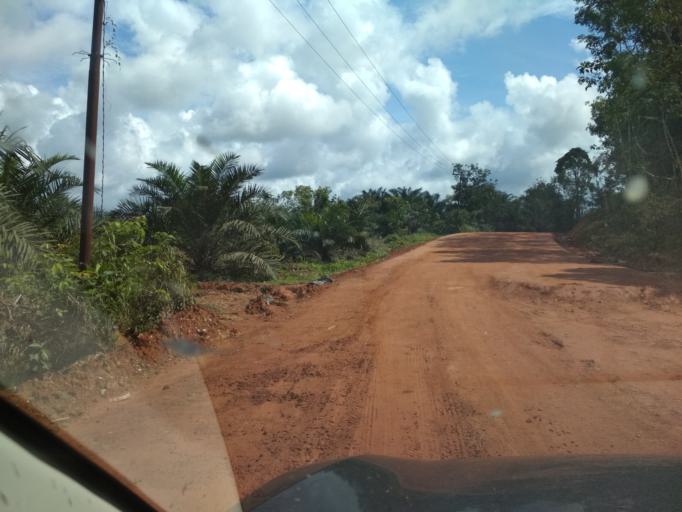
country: ID
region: West Kalimantan
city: Tayan
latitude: 0.5457
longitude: 110.0909
